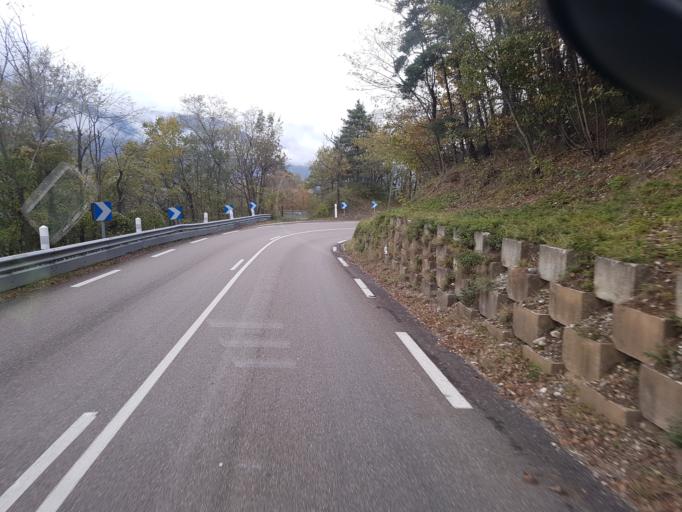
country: FR
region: Rhone-Alpes
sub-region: Departement de l'Isere
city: Le Gua
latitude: 44.9633
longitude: 5.6359
